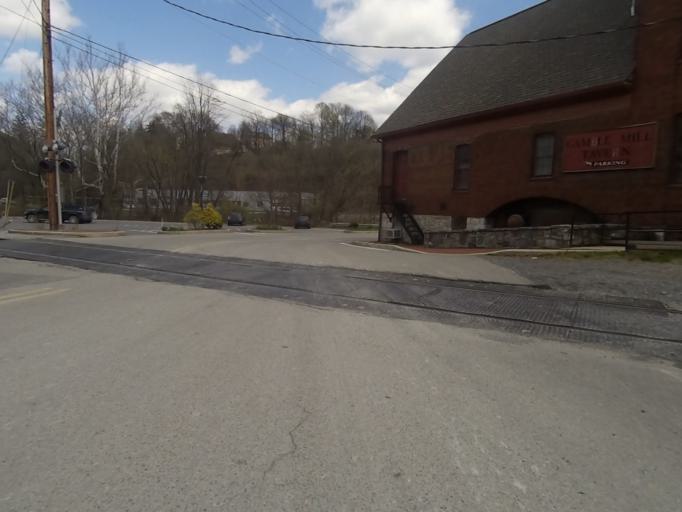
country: US
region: Pennsylvania
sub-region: Centre County
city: Bellefonte
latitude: 40.9139
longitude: -77.7836
